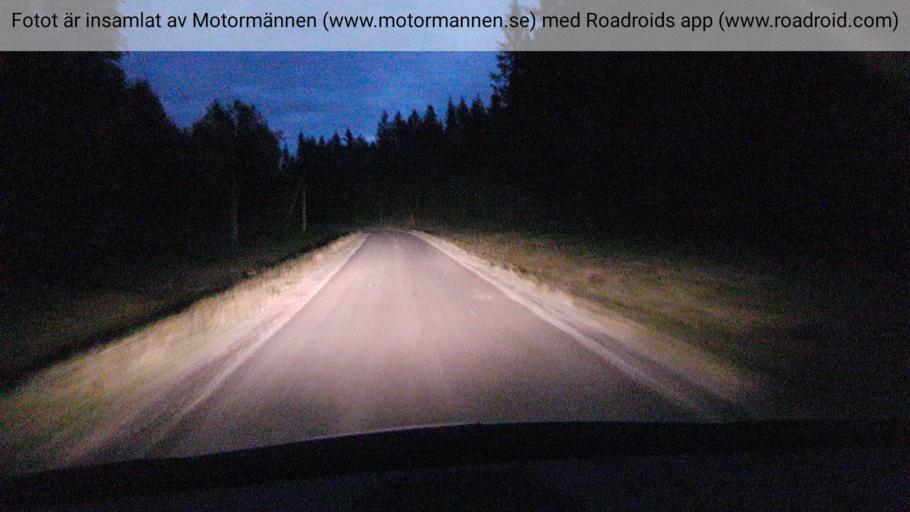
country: SE
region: Jaemtland
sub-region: OEstersunds Kommun
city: Lit
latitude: 63.3144
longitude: 15.2374
